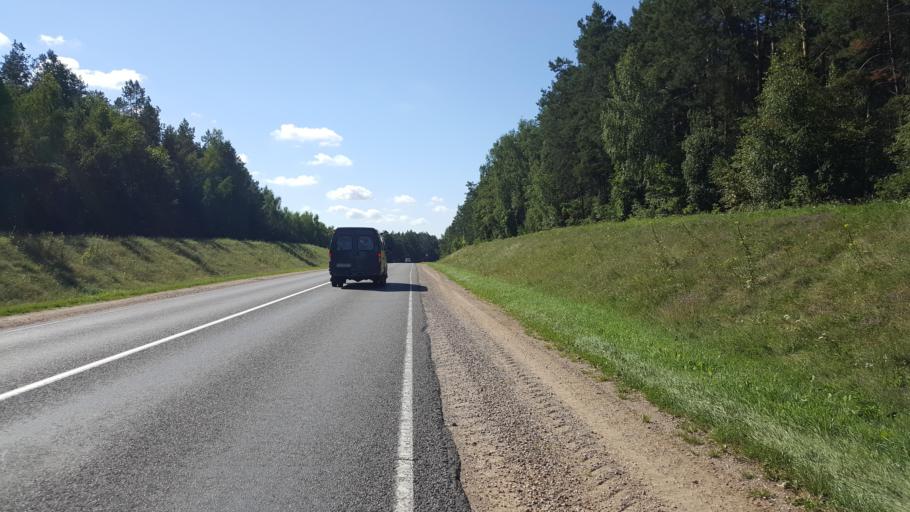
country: BY
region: Brest
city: Kamyanyets
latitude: 52.3469
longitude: 23.7788
